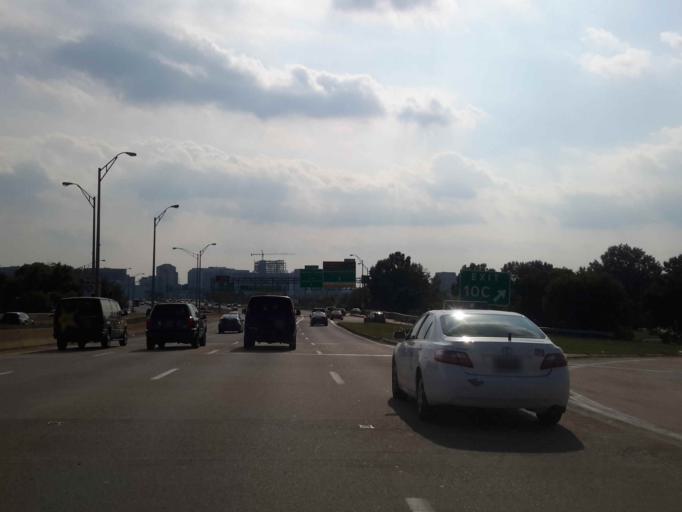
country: US
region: Washington, D.C.
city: Washington, D.C.
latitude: 38.8742
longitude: -77.0440
